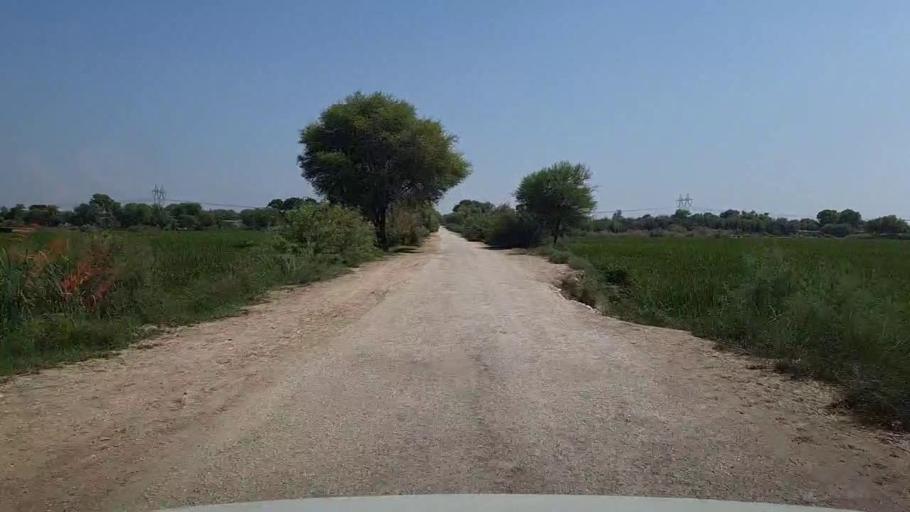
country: PK
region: Sindh
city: Kandhkot
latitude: 28.2904
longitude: 69.3521
